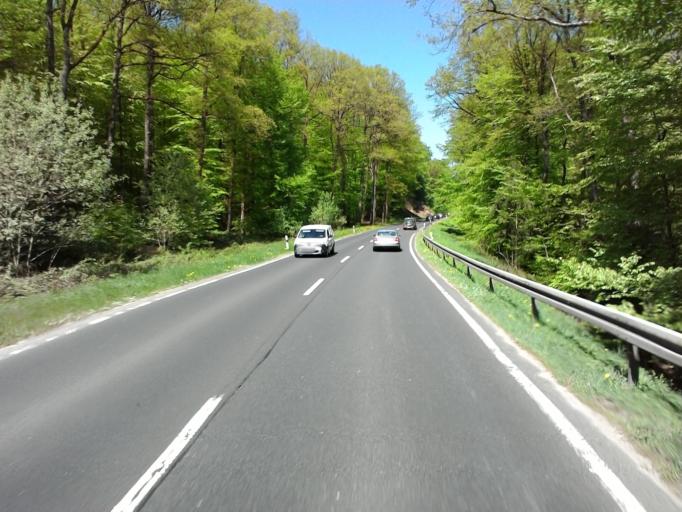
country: DE
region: Bavaria
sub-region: Regierungsbezirk Unterfranken
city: Rothenbuch
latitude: 49.9884
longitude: 9.3899
